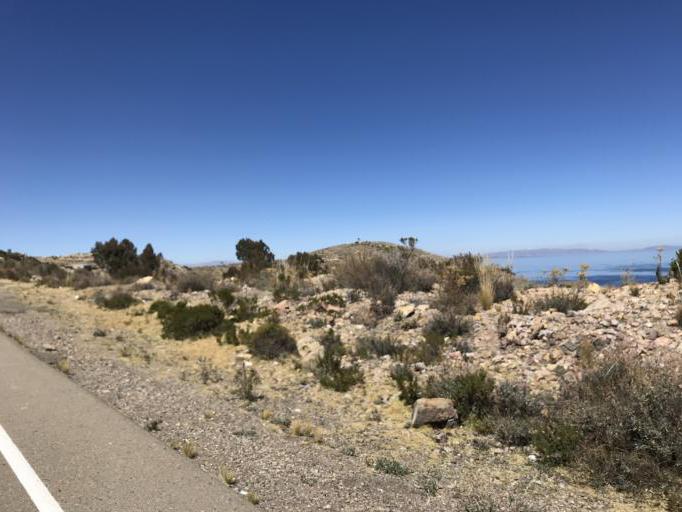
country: BO
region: La Paz
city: San Pedro
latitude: -16.1981
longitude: -68.9102
